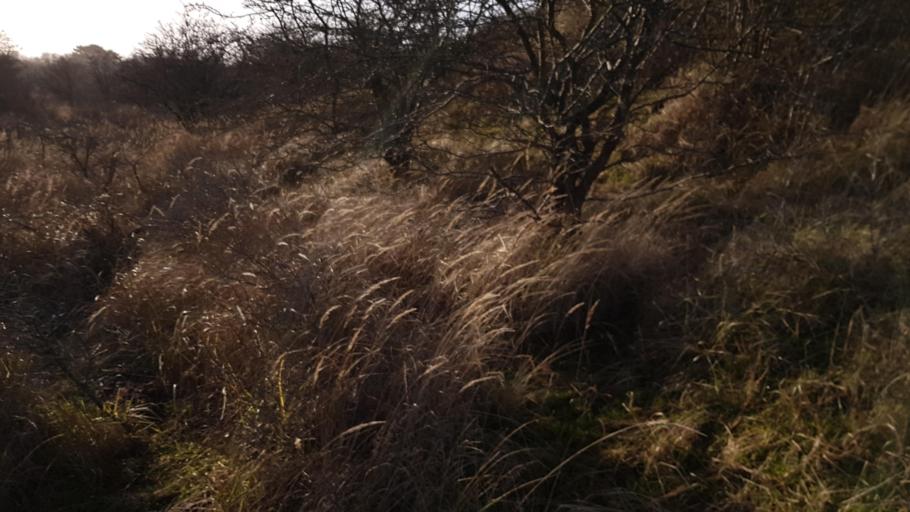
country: NL
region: North Holland
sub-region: Gemeente Bloemendaal
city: Bloemendaal
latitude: 52.4031
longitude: 4.5808
